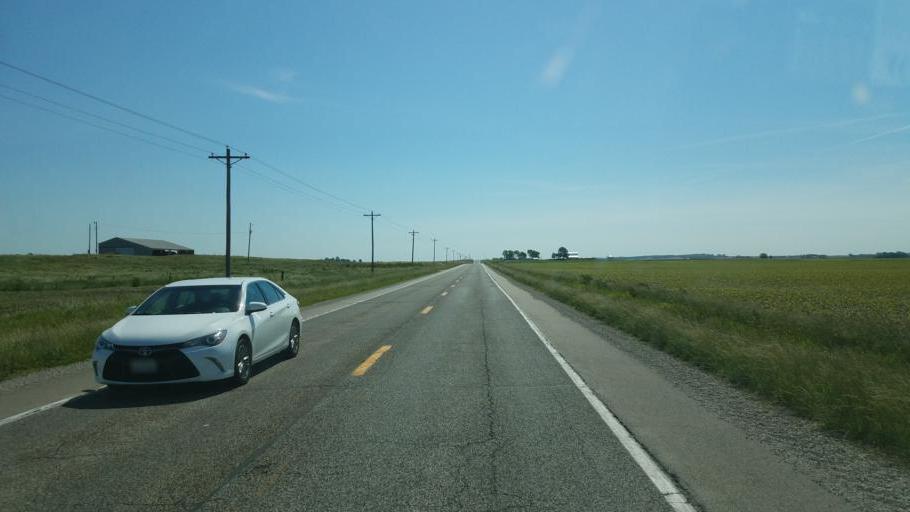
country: US
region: Illinois
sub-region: Mason County
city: Mason City
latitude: 40.3038
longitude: -89.7666
